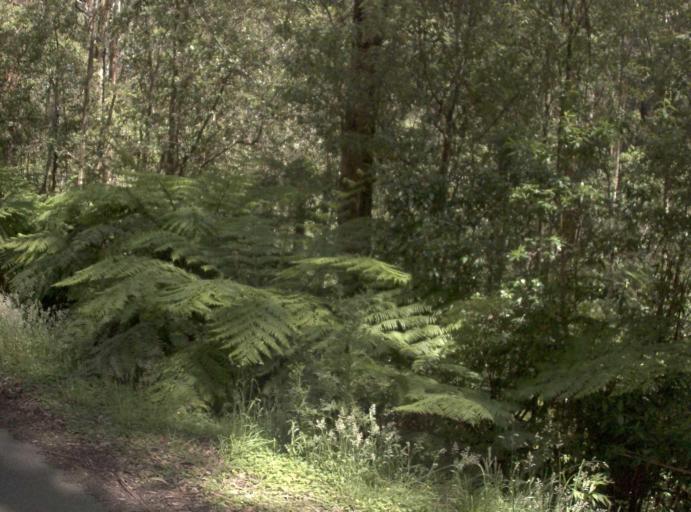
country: AU
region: Victoria
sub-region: Baw Baw
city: Warragul
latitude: -37.8594
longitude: 146.1093
